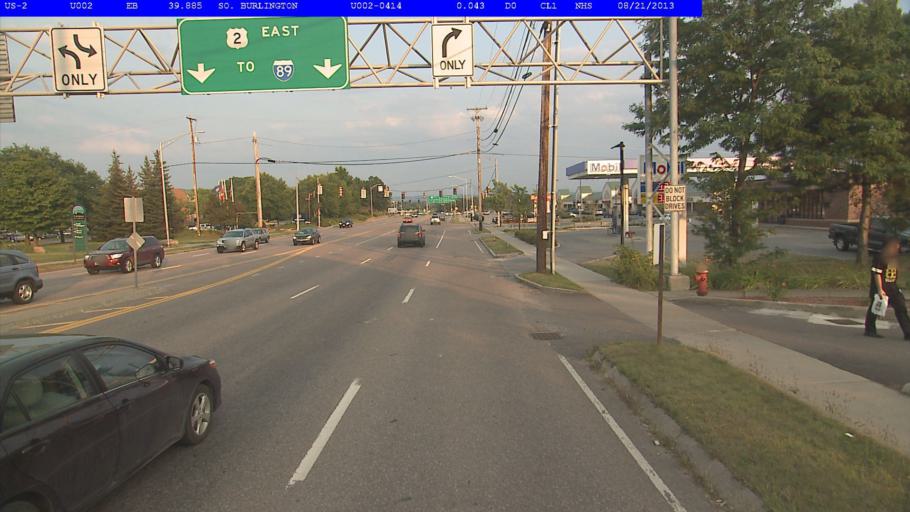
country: US
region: Vermont
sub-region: Chittenden County
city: South Burlington
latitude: 44.4721
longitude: -73.1895
